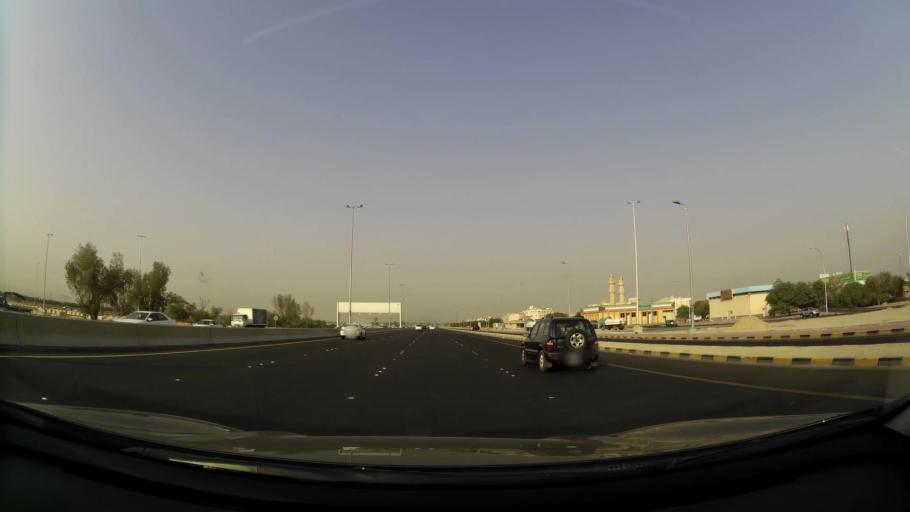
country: KW
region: Al Asimah
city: Ar Rabiyah
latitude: 29.3111
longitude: 47.8464
